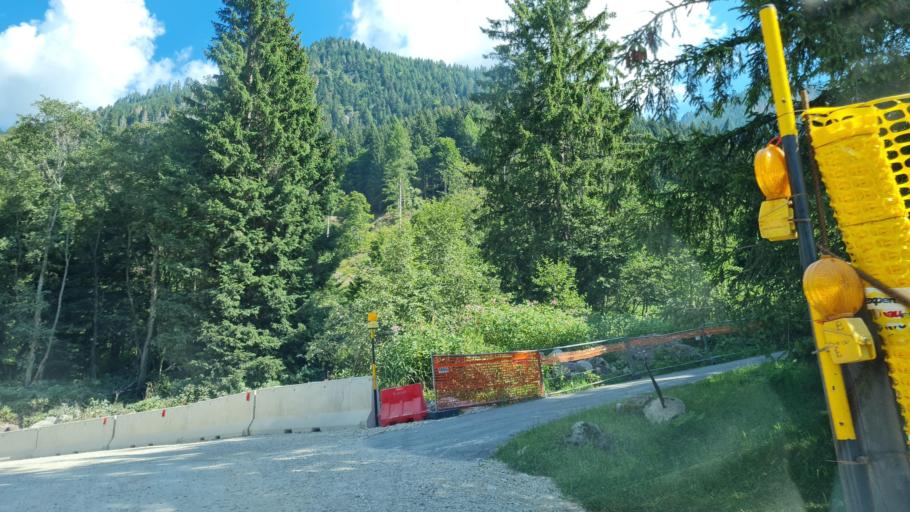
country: IT
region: Trentino-Alto Adige
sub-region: Provincia di Trento
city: Torcegno
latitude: 46.1402
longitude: 11.4686
